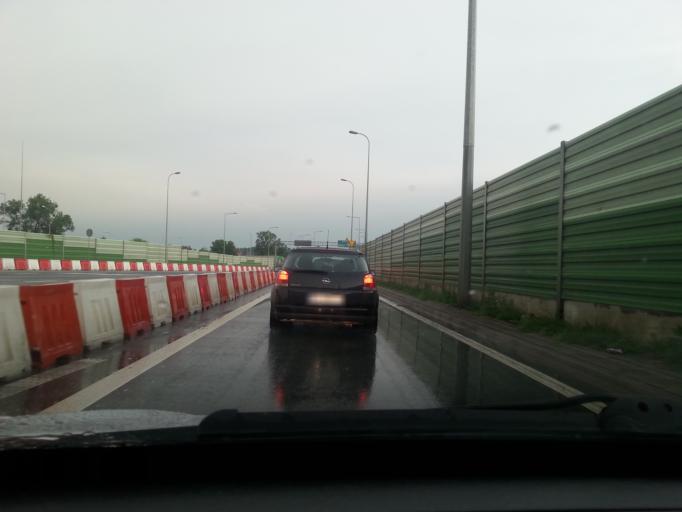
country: PL
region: Lodz Voivodeship
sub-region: Powiat zgierski
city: Strykow
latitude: 51.8846
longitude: 19.5836
